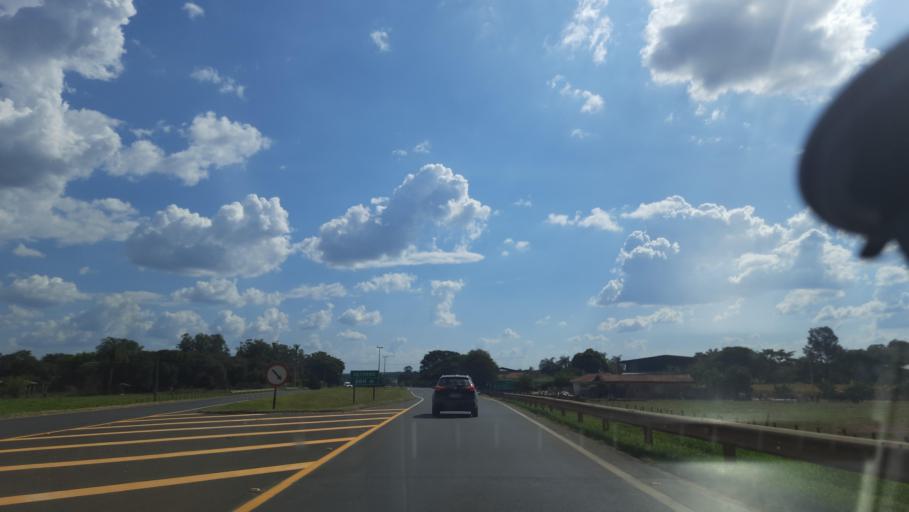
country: BR
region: Sao Paulo
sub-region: Casa Branca
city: Casa Branca
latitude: -21.7412
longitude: -46.9789
